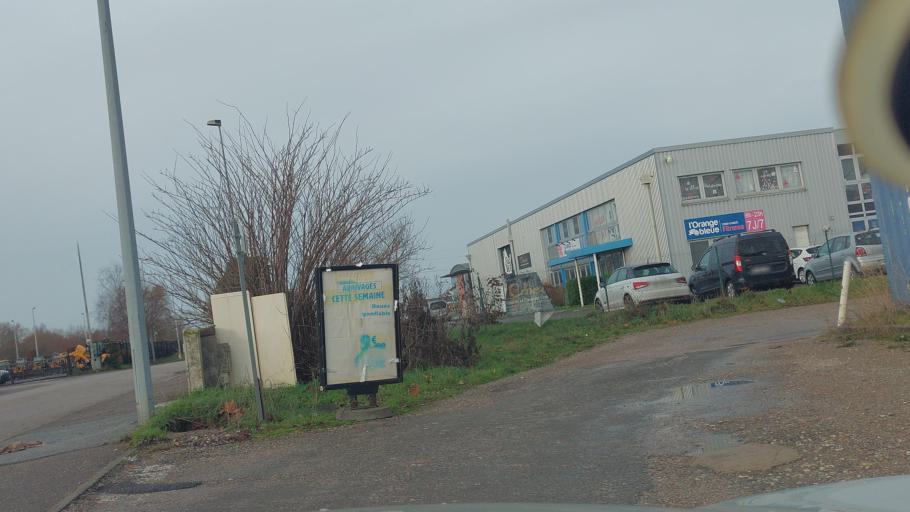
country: FR
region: Haute-Normandie
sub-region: Departement de la Seine-Maritime
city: Eu
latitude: 50.0582
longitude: 1.4122
